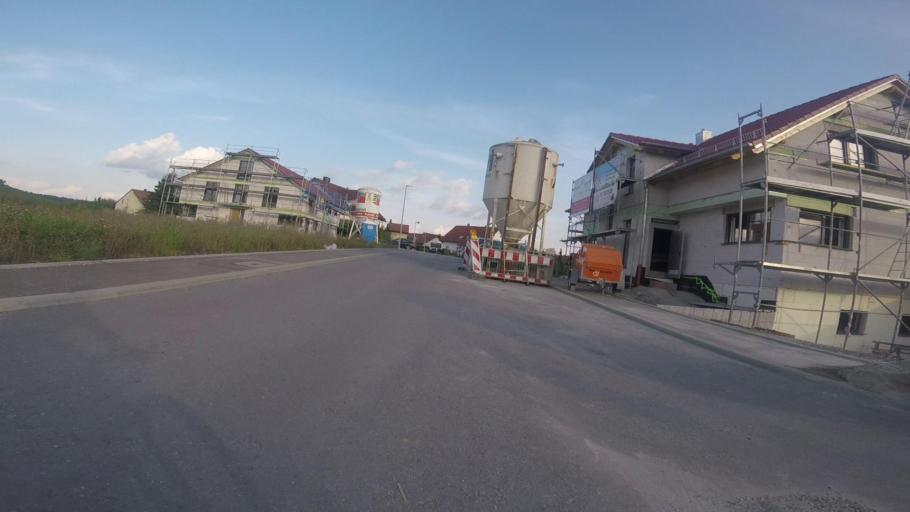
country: DE
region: Baden-Wuerttemberg
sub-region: Regierungsbezirk Stuttgart
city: Oberstenfeld
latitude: 48.9948
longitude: 9.3539
